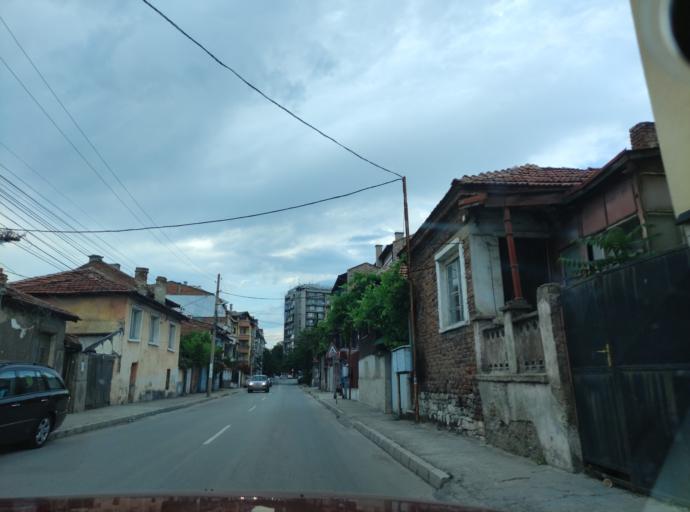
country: BG
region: Pazardzhik
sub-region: Obshtina Pazardzhik
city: Pazardzhik
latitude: 42.1846
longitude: 24.3349
